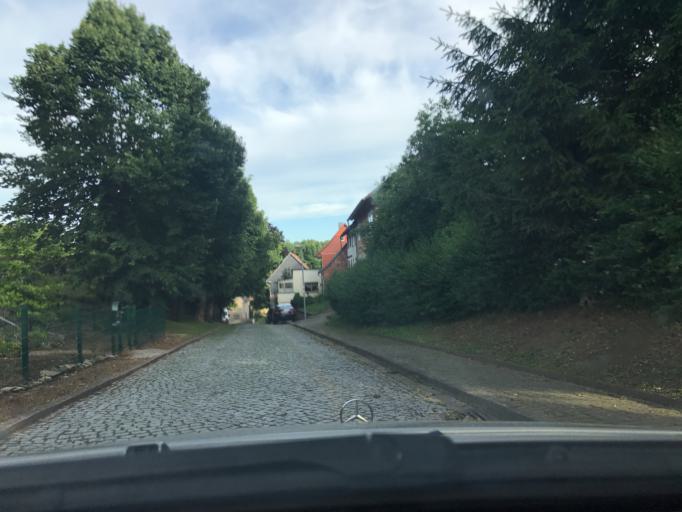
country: DE
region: Thuringia
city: Anrode
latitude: 51.2383
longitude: 10.3641
